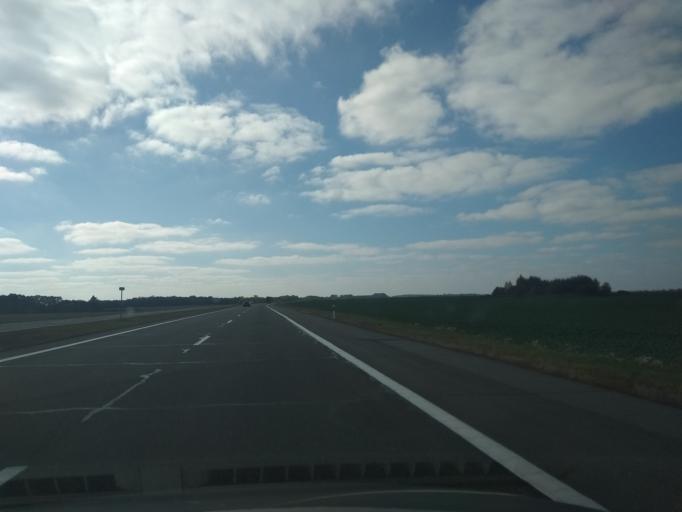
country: BY
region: Brest
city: Baranovichi
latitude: 53.2249
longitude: 26.1589
